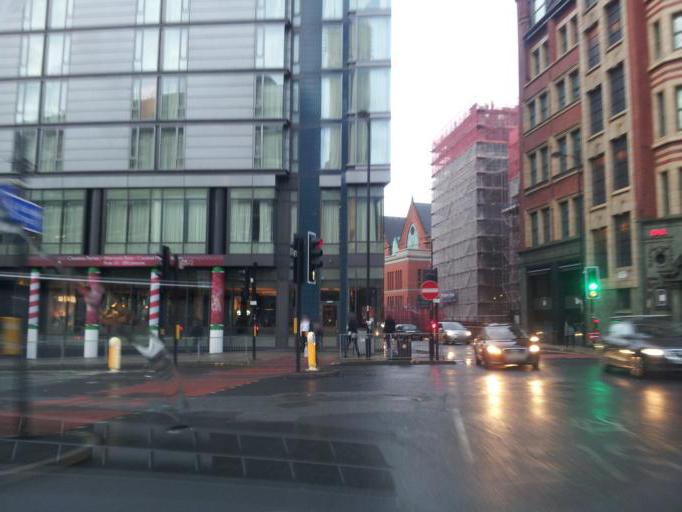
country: GB
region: England
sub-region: Manchester
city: Manchester
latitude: 53.4792
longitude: -2.2325
